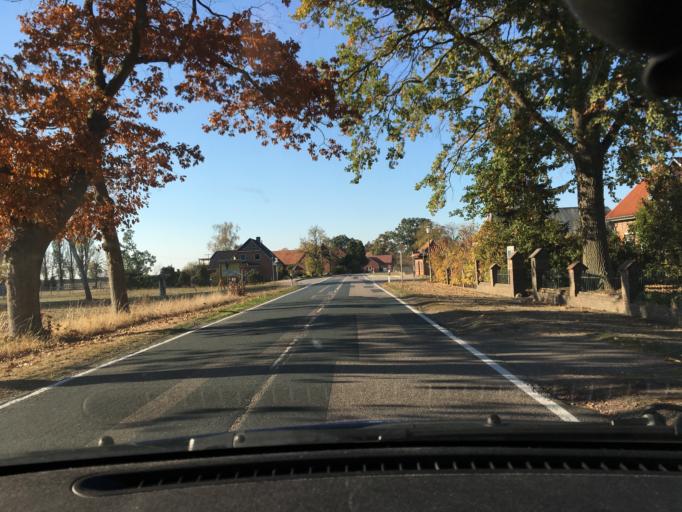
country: DE
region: Lower Saxony
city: Damnatz
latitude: 53.1711
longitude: 11.1679
